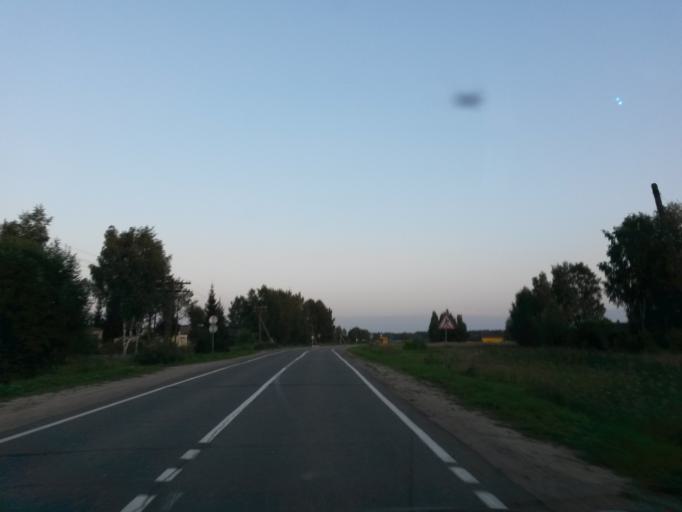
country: RU
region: Jaroslavl
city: Tutayev
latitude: 57.9392
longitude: 39.4984
